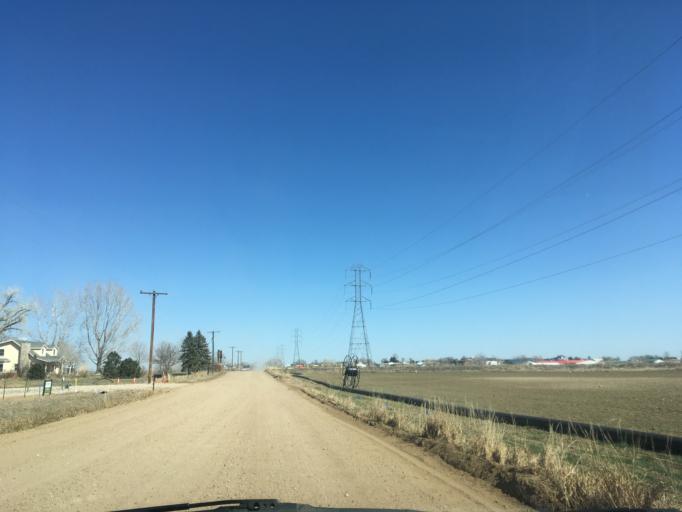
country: US
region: Colorado
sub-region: Boulder County
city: Erie
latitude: 40.0584
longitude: -105.0117
